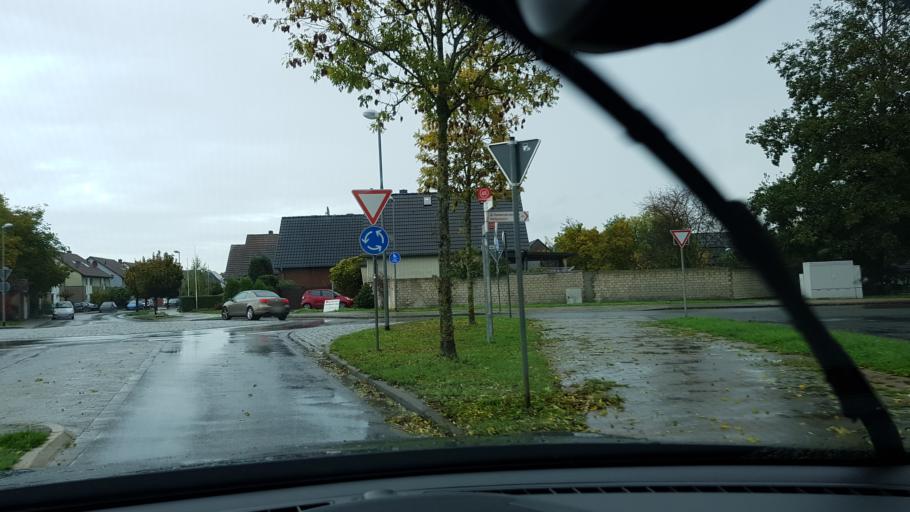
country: DE
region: North Rhine-Westphalia
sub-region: Regierungsbezirk Dusseldorf
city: Rommerskirchen
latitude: 51.0653
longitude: 6.6624
